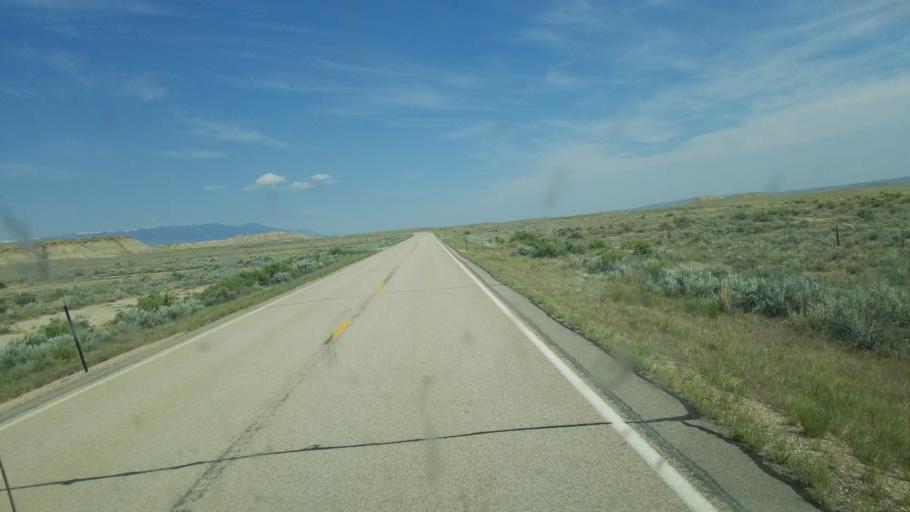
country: US
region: Wyoming
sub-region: Park County
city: Powell
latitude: 44.8276
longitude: -108.9776
